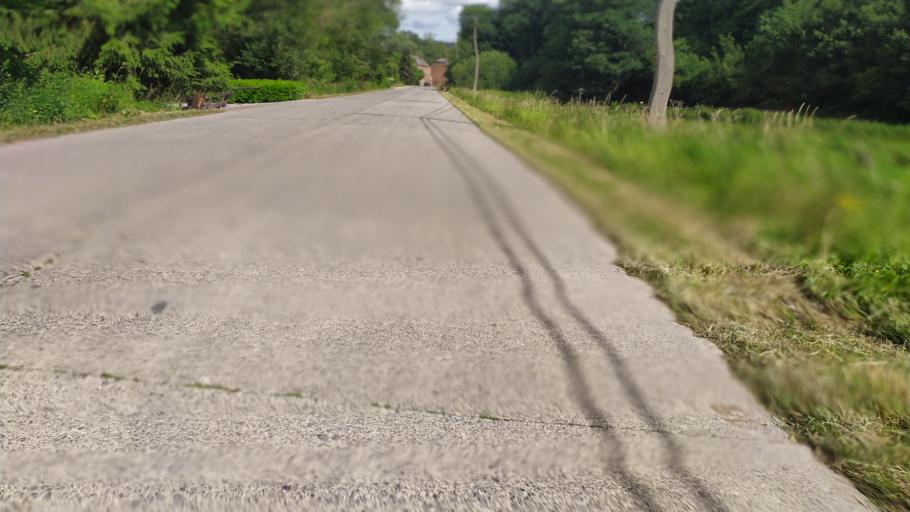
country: BE
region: Wallonia
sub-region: Province de Namur
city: Houyet
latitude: 50.1676
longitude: 5.0467
